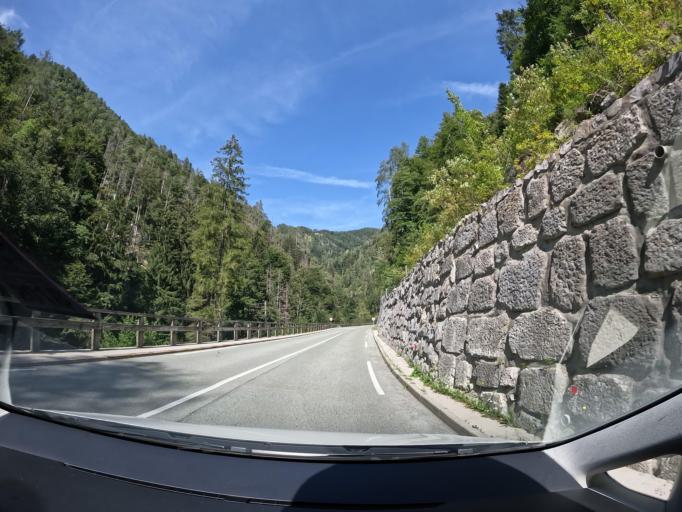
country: SI
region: Trzic
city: Trzic
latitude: 46.4159
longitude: 14.2943
